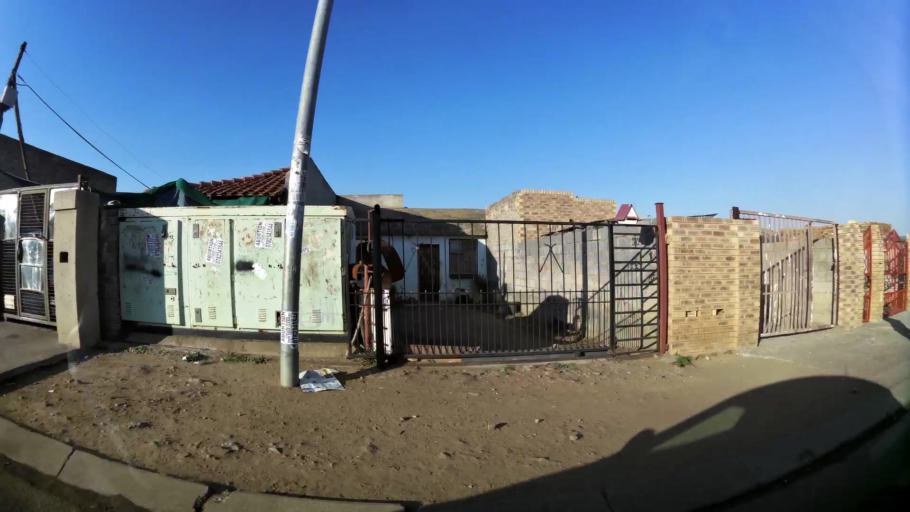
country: ZA
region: Gauteng
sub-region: City of Johannesburg Metropolitan Municipality
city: Soweto
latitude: -26.2530
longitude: 27.8842
